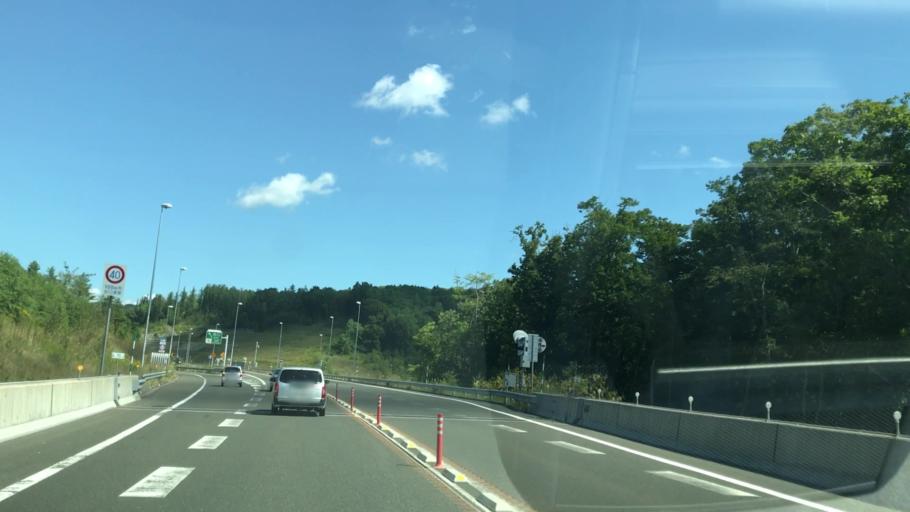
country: JP
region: Hokkaido
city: Shimo-furano
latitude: 42.9774
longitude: 142.4070
